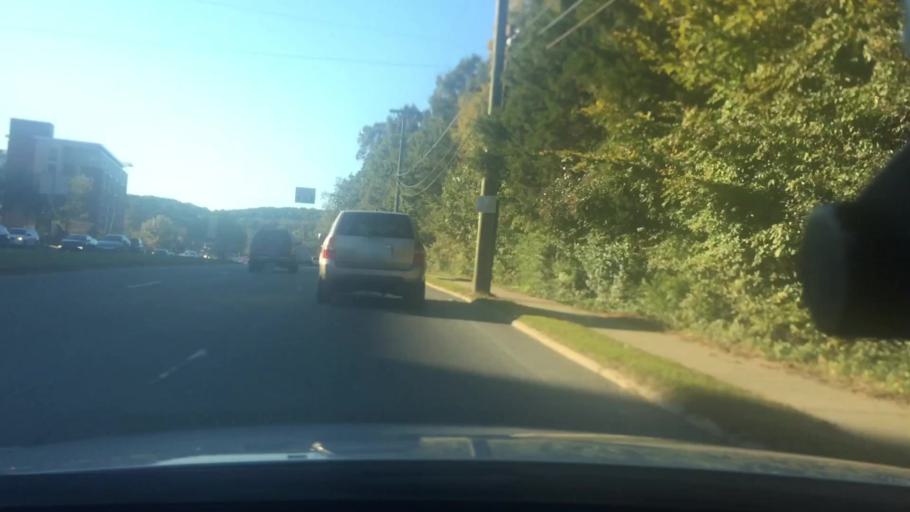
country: US
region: North Carolina
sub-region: Orange County
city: Chapel Hill
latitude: 35.9074
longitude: -79.0212
